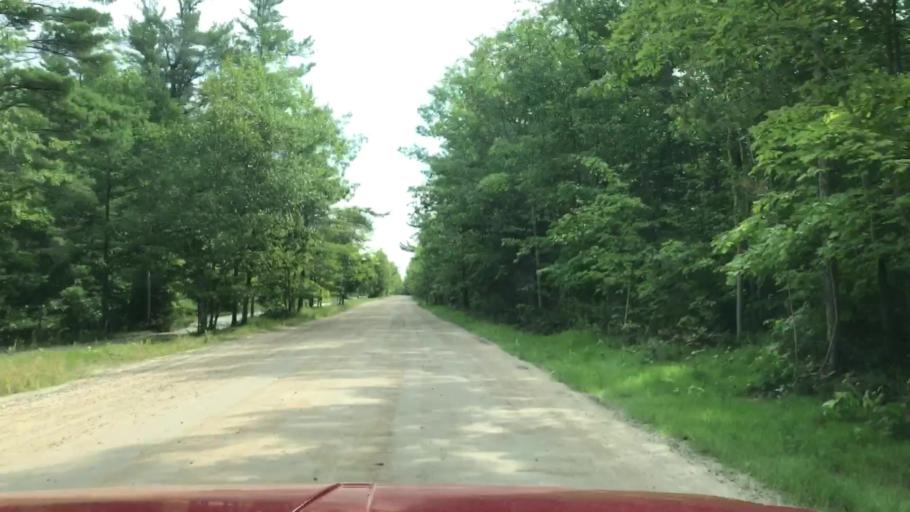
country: US
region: Michigan
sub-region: Charlevoix County
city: Charlevoix
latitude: 45.7468
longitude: -85.5336
